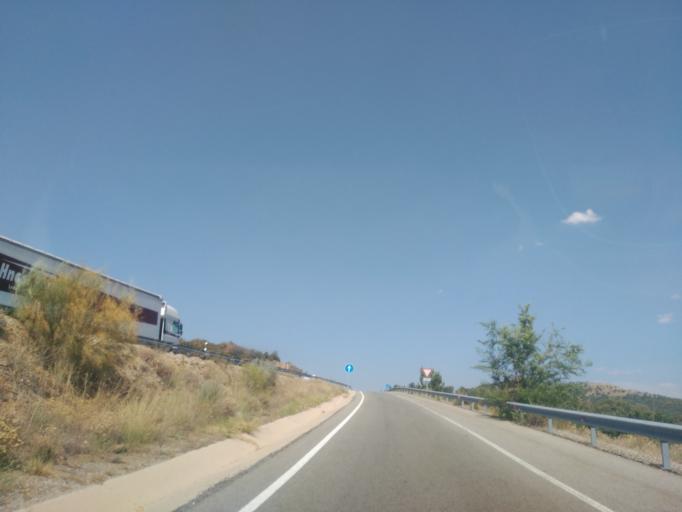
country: ES
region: Castille and Leon
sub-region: Provincia de Salamanca
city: Vallejera de Riofrio
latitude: 40.3994
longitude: -5.7356
